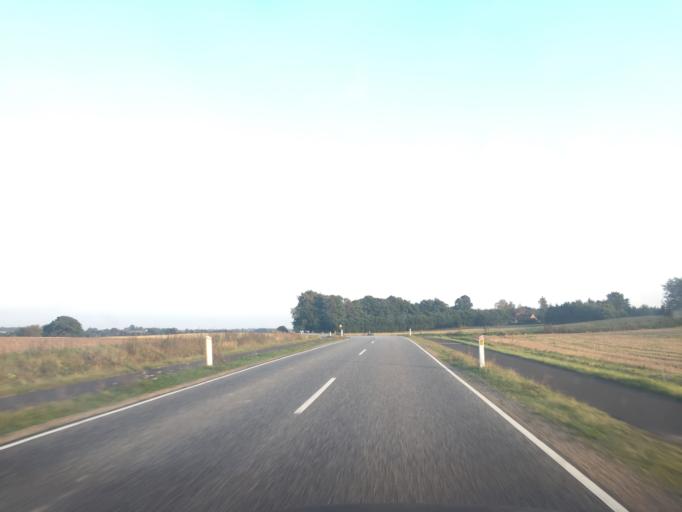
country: DK
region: Zealand
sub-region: Lejre Kommune
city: Kirke Hvalso
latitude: 55.5855
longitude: 11.8828
